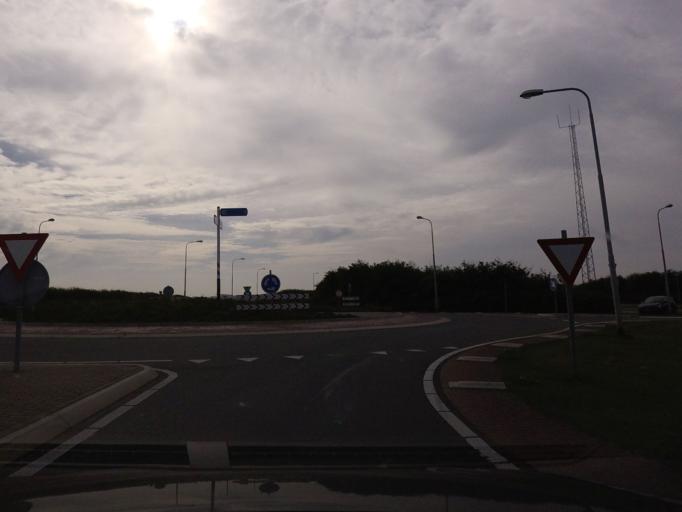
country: NL
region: North Holland
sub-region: Gemeente Den Helder
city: Den Helder
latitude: 52.8622
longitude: 4.7109
